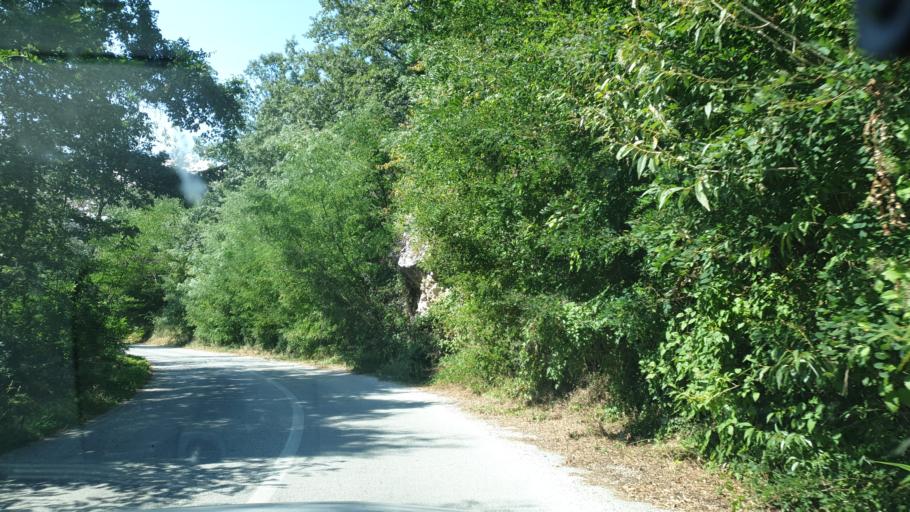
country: RS
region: Central Serbia
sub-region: Zlatiborski Okrug
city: Cajetina
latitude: 43.6758
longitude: 19.8369
